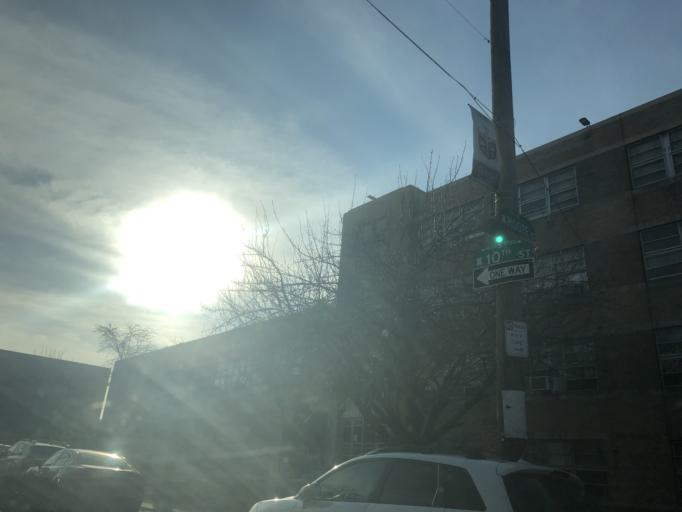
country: US
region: Pennsylvania
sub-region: Philadelphia County
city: Philadelphia
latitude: 39.9271
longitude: -75.1621
